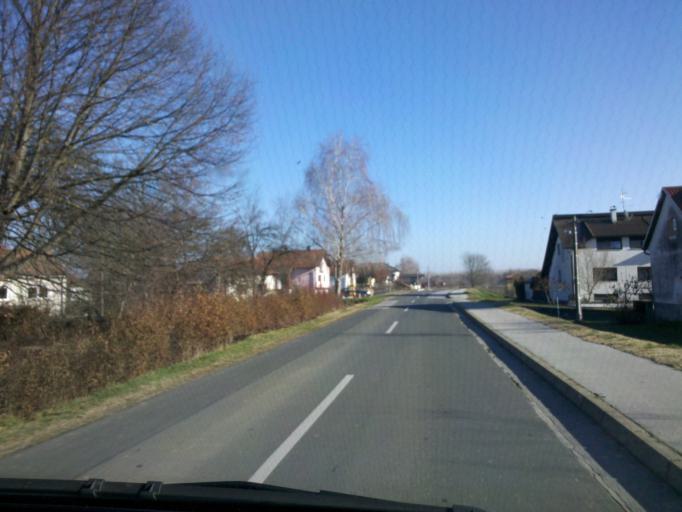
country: HR
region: Medimurska
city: Kotoriba
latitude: 46.3316
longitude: 16.7943
